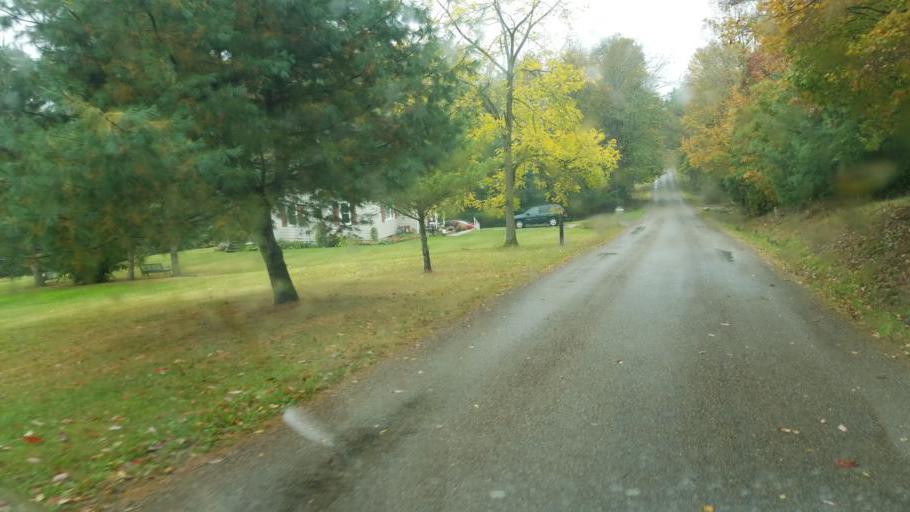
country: US
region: Ohio
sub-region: Sandusky County
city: Bellville
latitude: 40.6669
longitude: -82.3969
